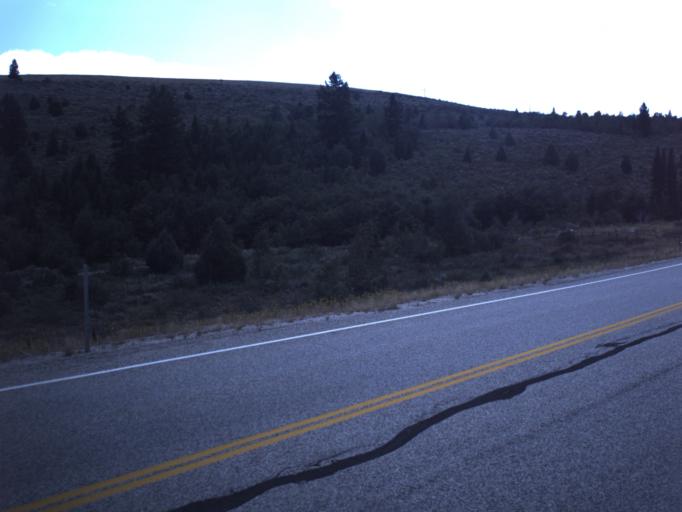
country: US
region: Idaho
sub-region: Bear Lake County
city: Paris
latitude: 41.9258
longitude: -111.4263
